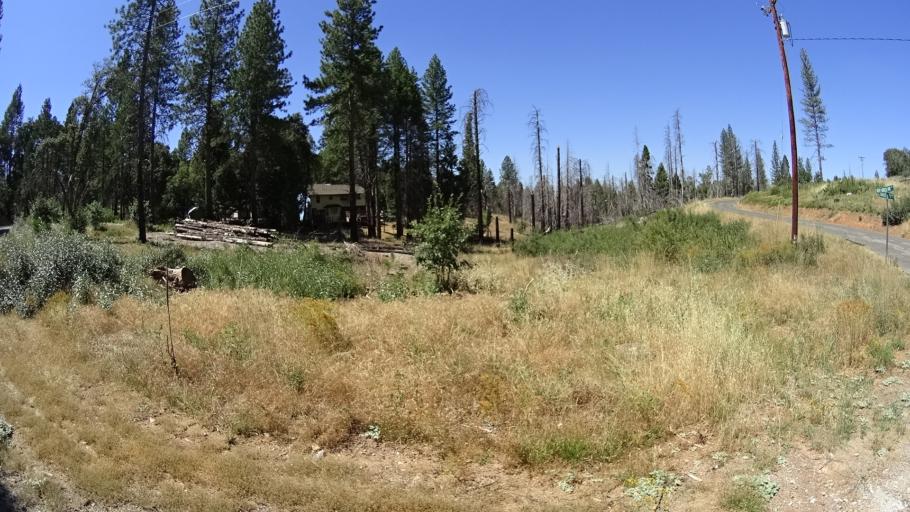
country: US
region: California
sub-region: Calaveras County
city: Mountain Ranch
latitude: 38.2761
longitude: -120.5485
